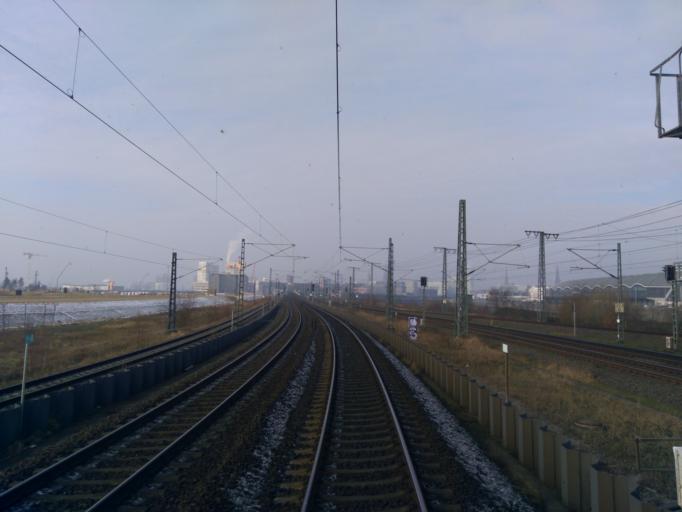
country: DE
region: Hamburg
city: Hammerbrook
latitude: 53.5389
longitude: 10.0220
